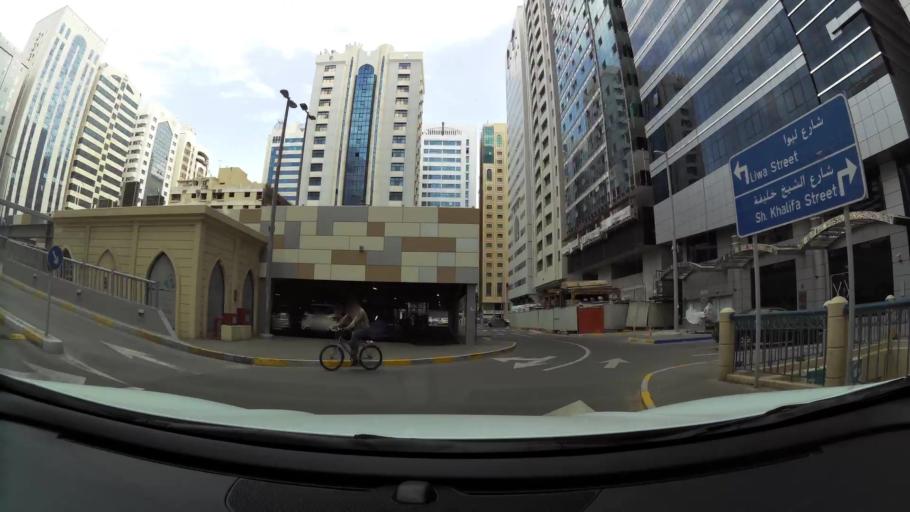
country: AE
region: Abu Dhabi
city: Abu Dhabi
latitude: 24.4897
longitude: 54.3601
